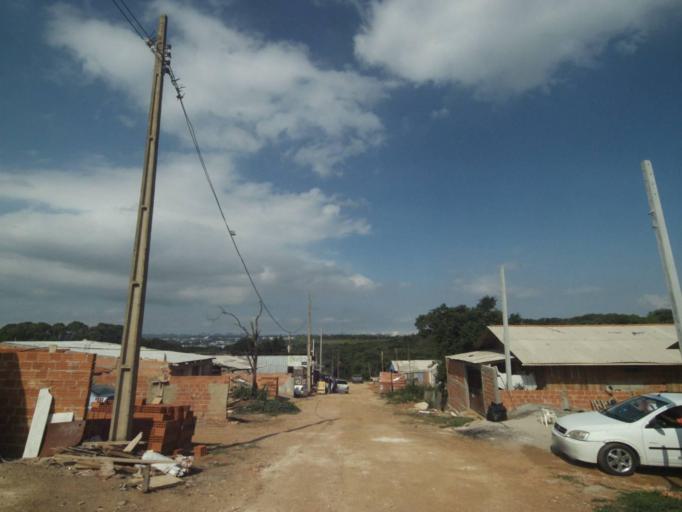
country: BR
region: Parana
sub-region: Araucaria
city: Araucaria
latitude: -25.5110
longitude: -49.3512
